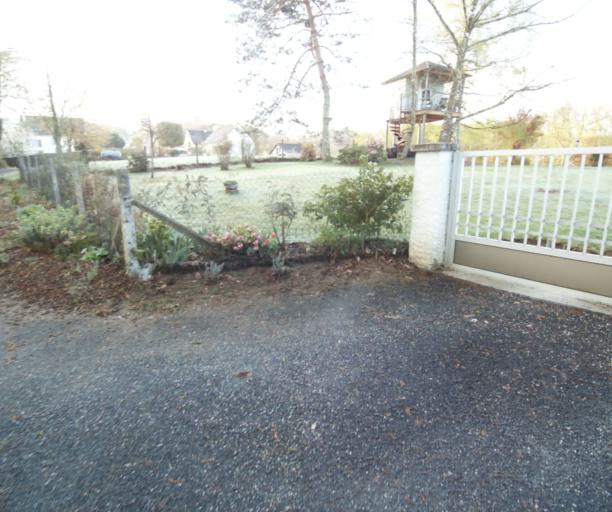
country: FR
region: Limousin
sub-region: Departement de la Correze
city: Naves
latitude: 45.3150
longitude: 1.8204
